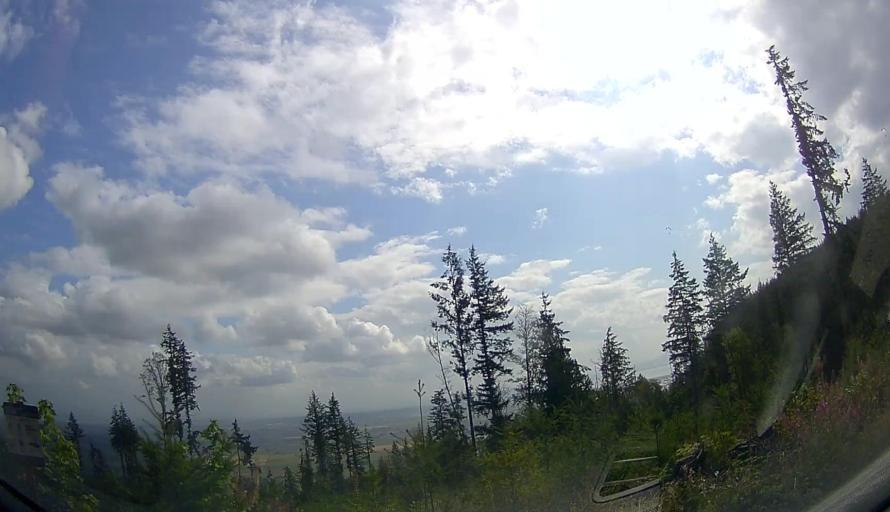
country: US
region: Washington
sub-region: Whatcom County
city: Sudden Valley
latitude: 48.6127
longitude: -122.4195
